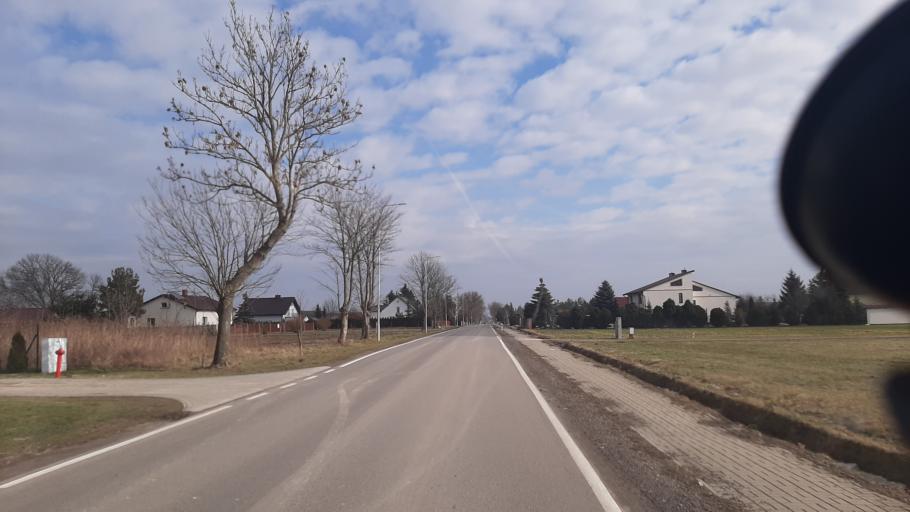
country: PL
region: Lublin Voivodeship
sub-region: Powiat lubelski
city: Niemce
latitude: 51.3614
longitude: 22.5727
